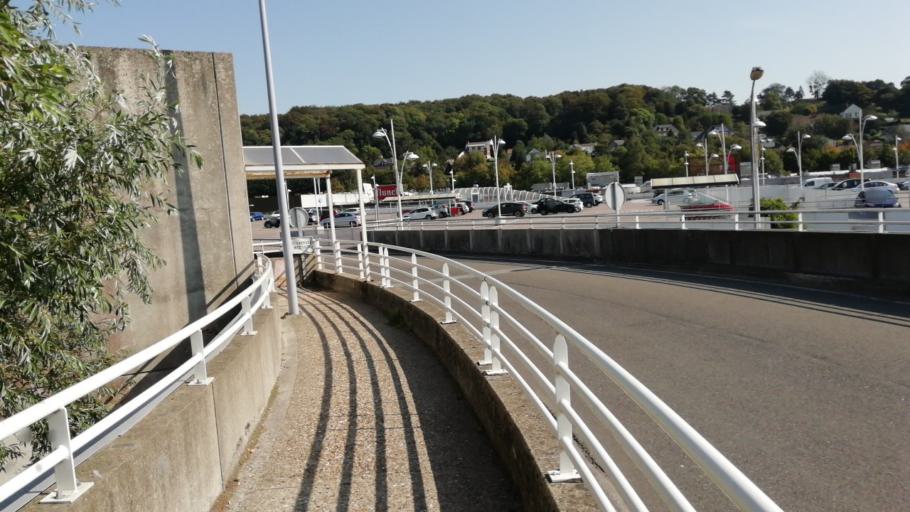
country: FR
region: Haute-Normandie
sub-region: Departement de la Seine-Maritime
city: Montivilliers
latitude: 49.5272
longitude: 0.1882
